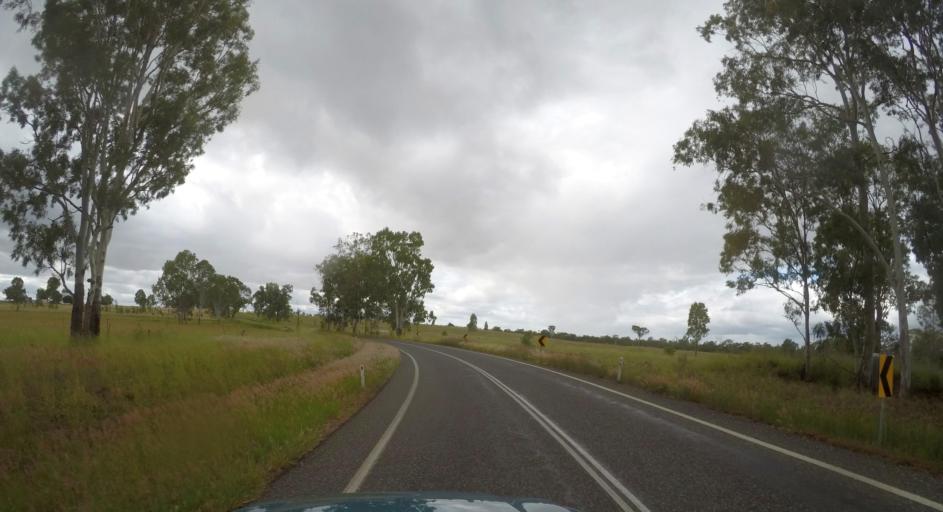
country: AU
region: Queensland
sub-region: North Burnett
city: Gayndah
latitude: -25.6726
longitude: 151.2475
